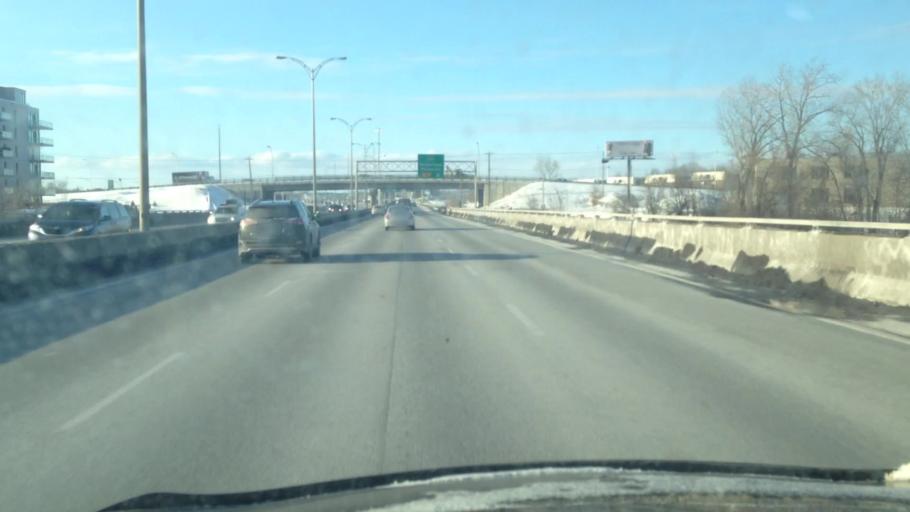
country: CA
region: Quebec
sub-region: Laurentides
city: Boisbriand
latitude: 45.6138
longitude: -73.8179
